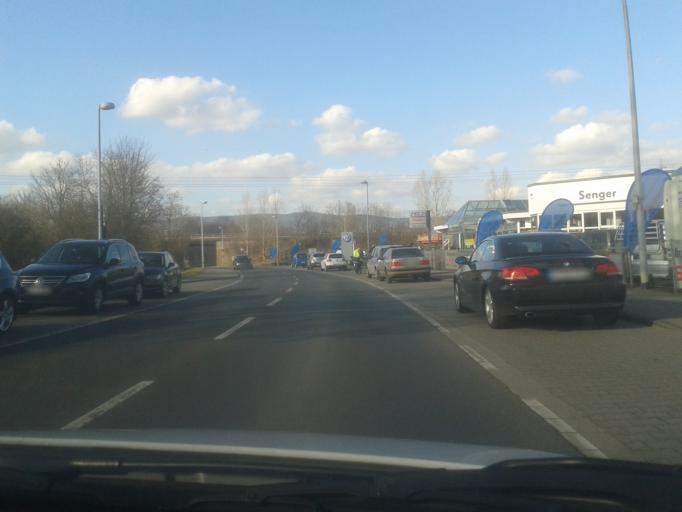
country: DE
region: Rheinland-Pfalz
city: Ingelheim am Rhein
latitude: 49.9843
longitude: 8.0509
